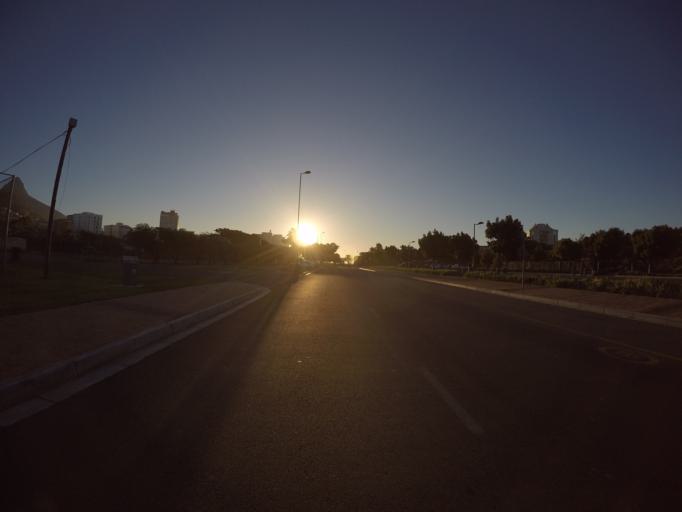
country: ZA
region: Western Cape
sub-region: City of Cape Town
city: Cape Town
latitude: -33.9056
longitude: 18.4018
